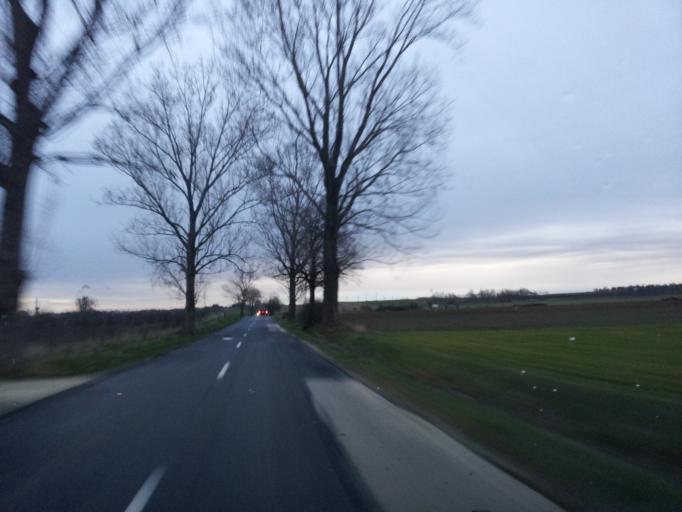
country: HU
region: Gyor-Moson-Sopron
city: Fertoszentmiklos
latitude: 47.5653
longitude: 16.8539
